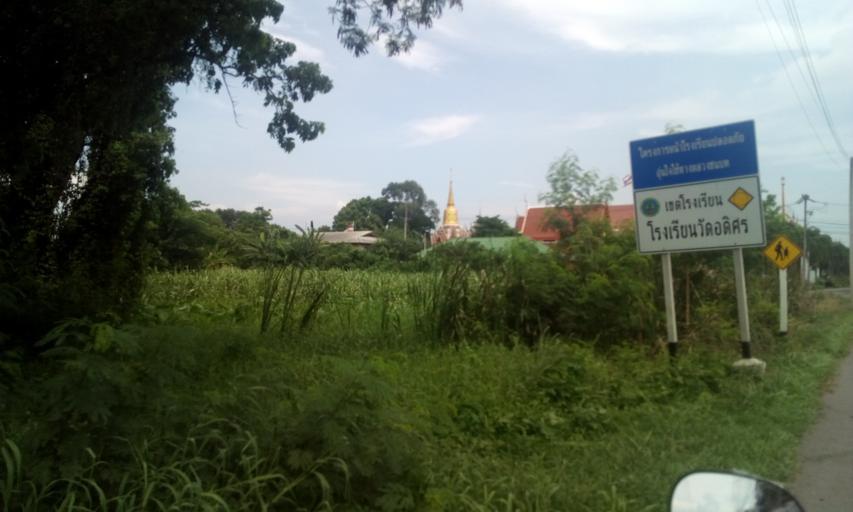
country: TH
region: Pathum Thani
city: Ban Lam Luk Ka
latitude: 14.0207
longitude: 100.8435
